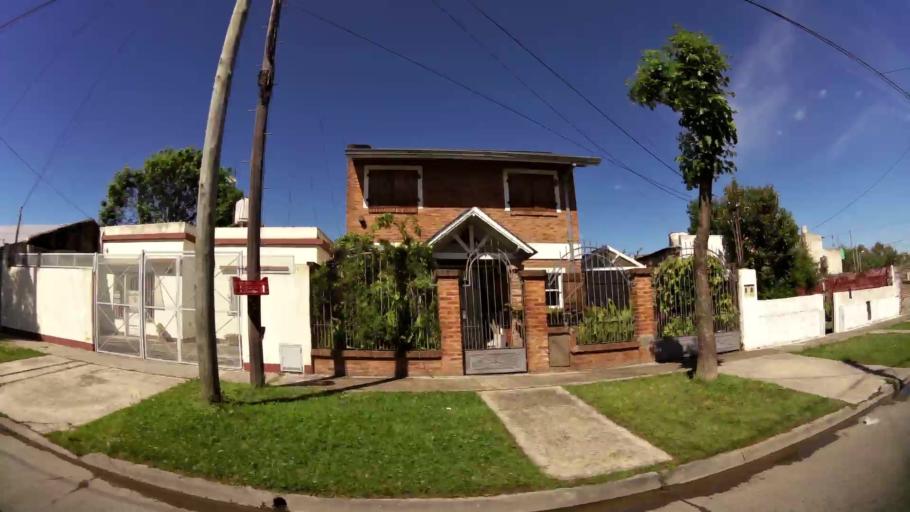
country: AR
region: Buenos Aires
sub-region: Partido de Quilmes
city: Quilmes
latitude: -34.6901
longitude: -58.3041
